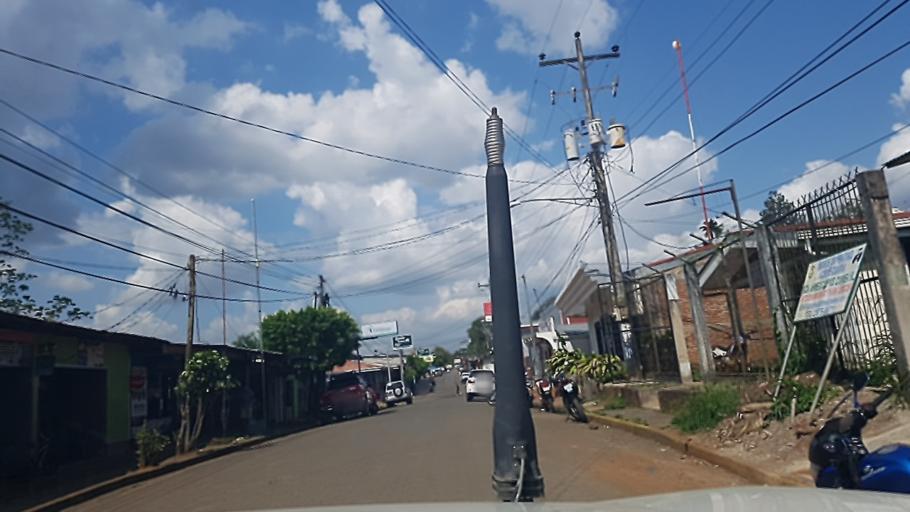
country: NI
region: Atlantico Sur
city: Nueva Guinea
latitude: 11.6885
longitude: -84.4563
